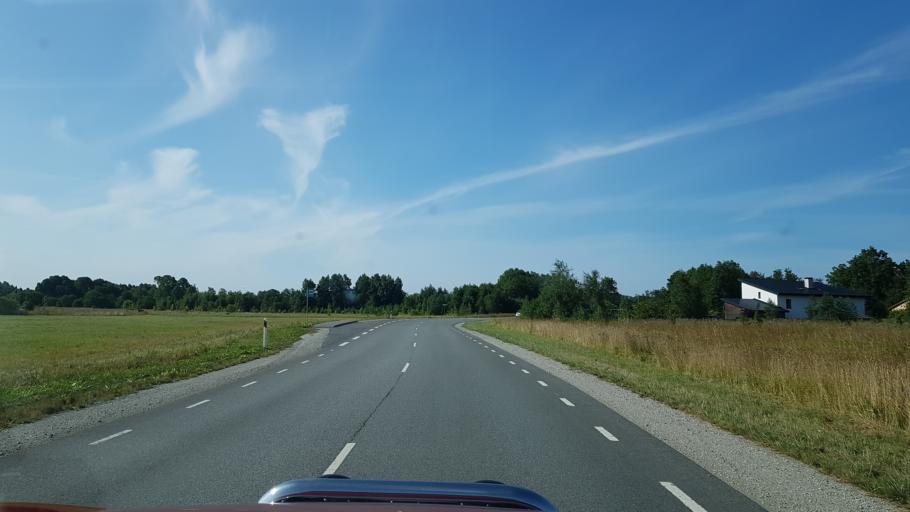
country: EE
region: Harju
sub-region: Rae vald
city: Jueri
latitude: 59.3737
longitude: 24.9251
